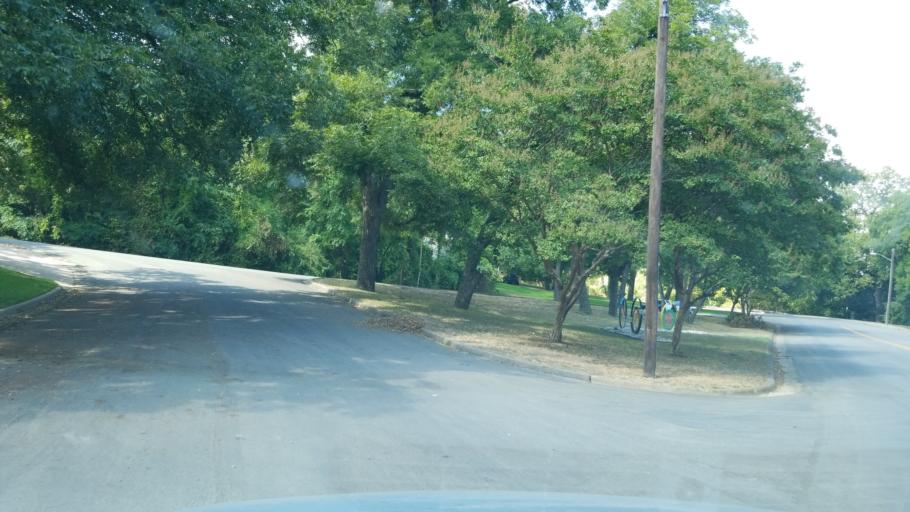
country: US
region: Texas
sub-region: Dallas County
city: Dallas
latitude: 32.7667
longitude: -96.8292
